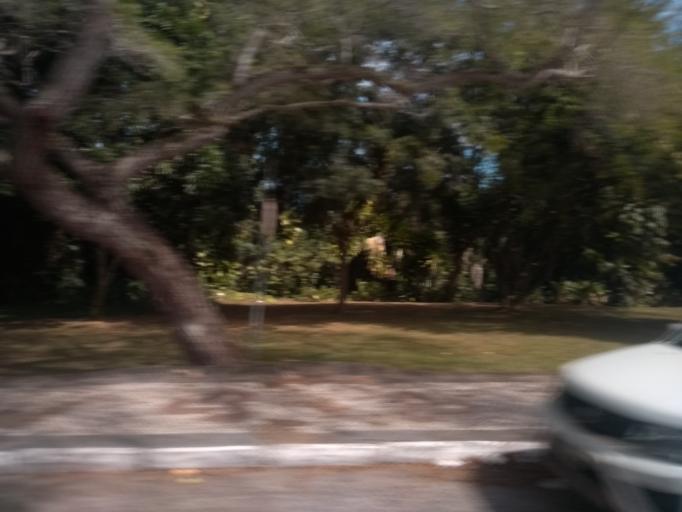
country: BR
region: Bahia
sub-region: Salvador
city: Salvador
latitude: -12.9447
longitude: -38.4272
